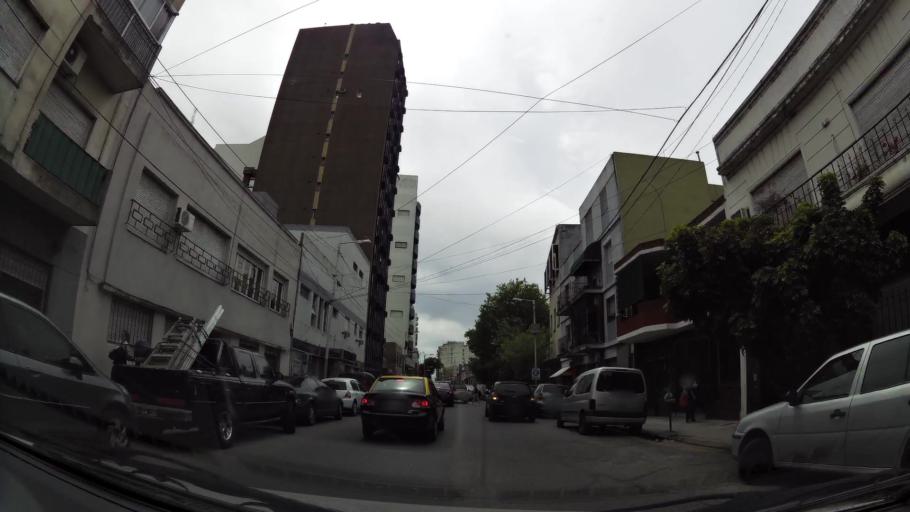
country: AR
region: Buenos Aires
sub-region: Partido de Avellaneda
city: Avellaneda
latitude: -34.6608
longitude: -58.3703
